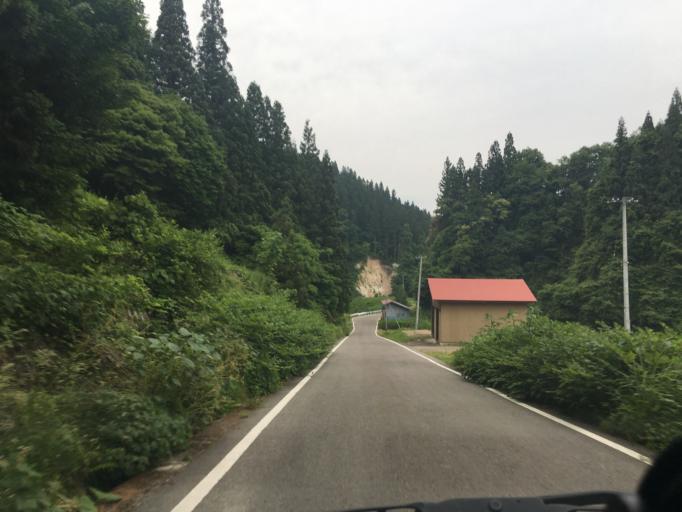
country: JP
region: Fukushima
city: Kitakata
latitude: 37.5047
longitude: 139.7381
